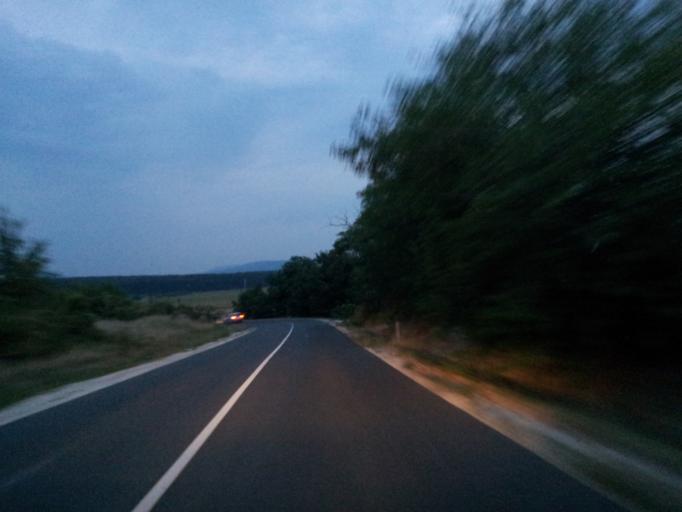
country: HU
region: Veszprem
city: Sumeg
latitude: 46.9743
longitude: 17.3016
